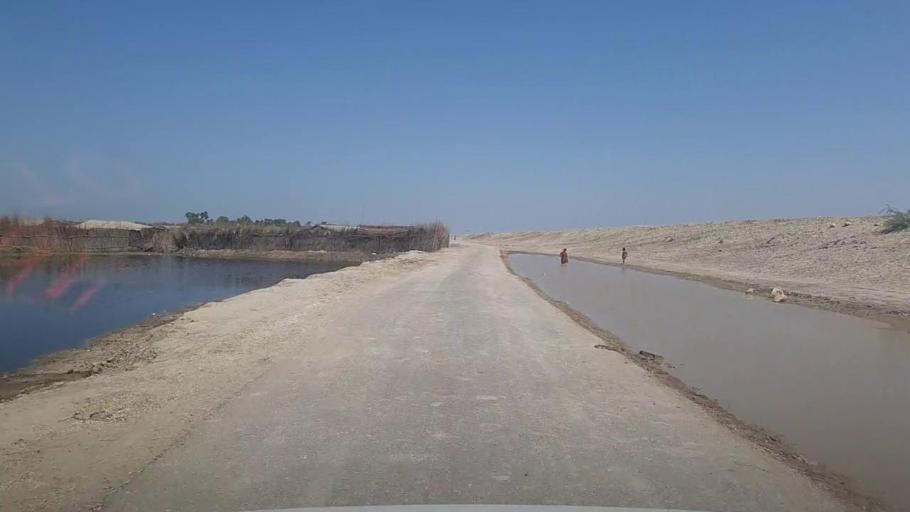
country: PK
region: Sindh
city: Kashmor
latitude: 28.2829
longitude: 69.4624
